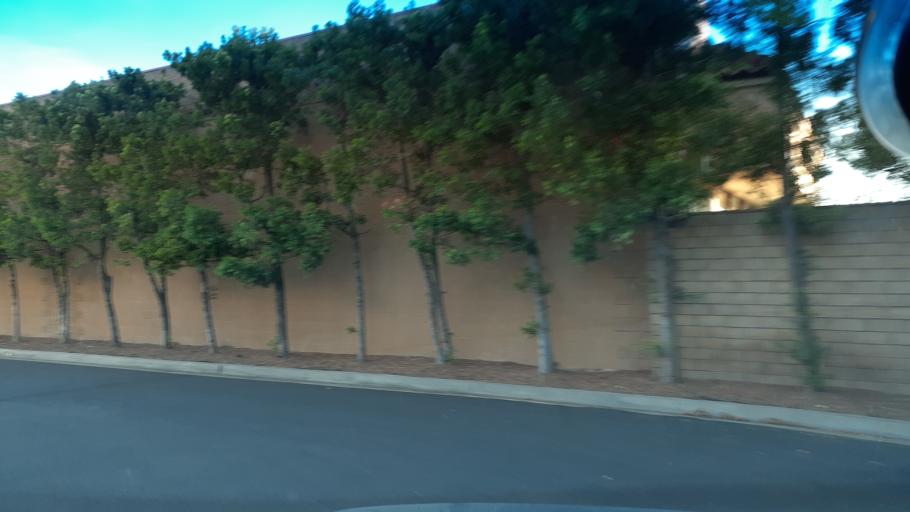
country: US
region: California
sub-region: Los Angeles County
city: Artesia
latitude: 33.8479
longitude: -118.0818
